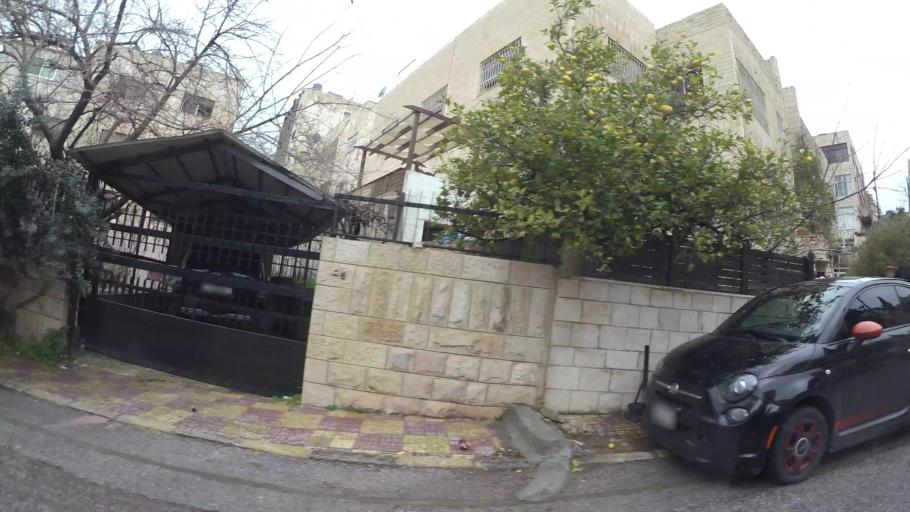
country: JO
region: Amman
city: Amman
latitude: 31.9500
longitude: 35.9103
